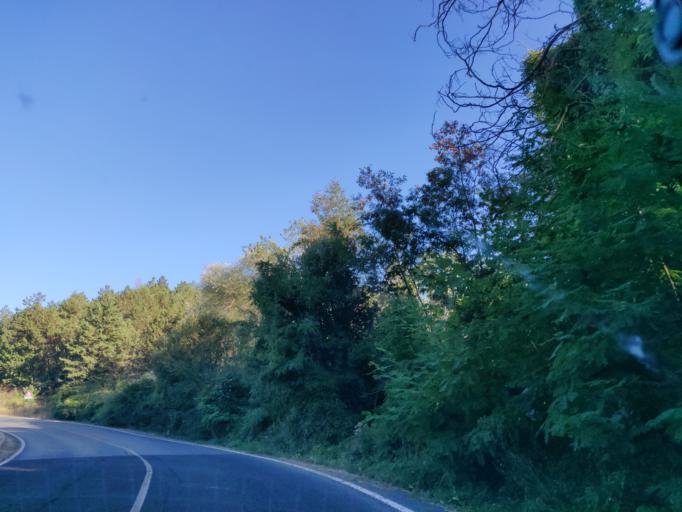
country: IT
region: Tuscany
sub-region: Provincia di Siena
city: Piancastagnaio
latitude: 42.8614
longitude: 11.6792
